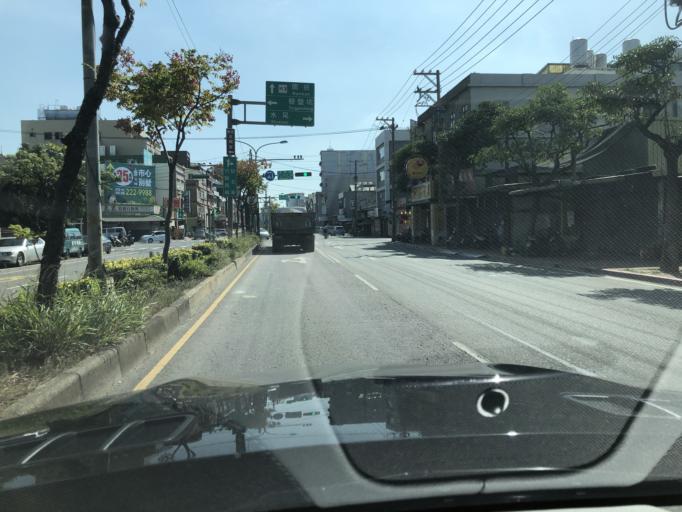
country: TW
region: Taiwan
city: Taoyuan City
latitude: 25.0740
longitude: 121.2852
